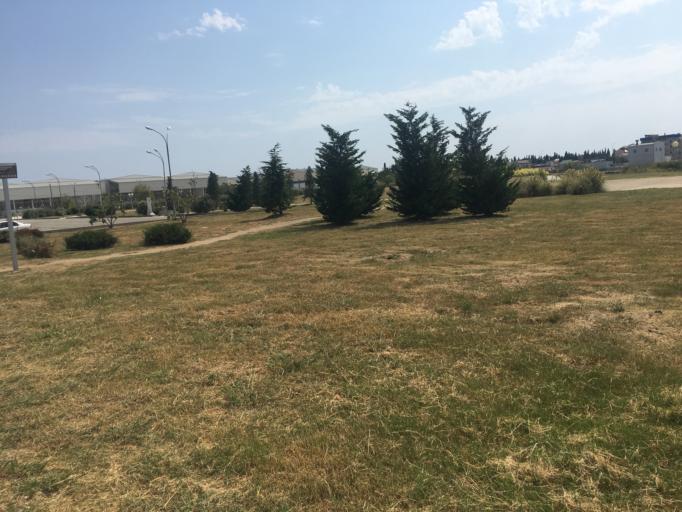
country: RU
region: Krasnodarskiy
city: Adler
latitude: 43.3989
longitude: 39.9815
